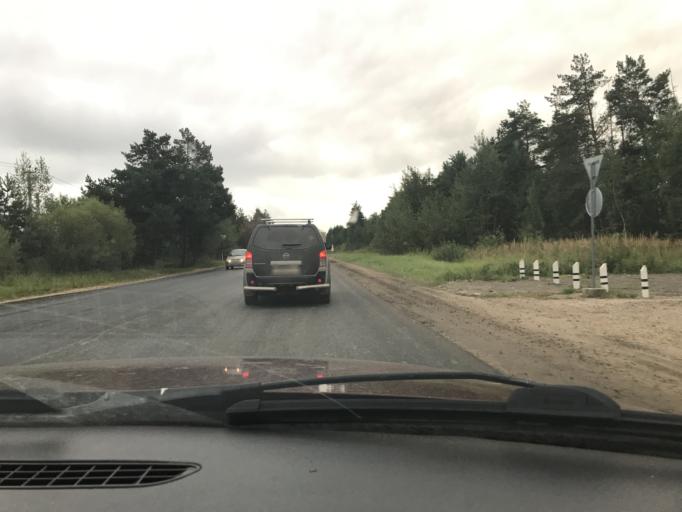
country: RU
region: Kaluga
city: Pyatovskiy
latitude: 54.6475
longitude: 36.0366
